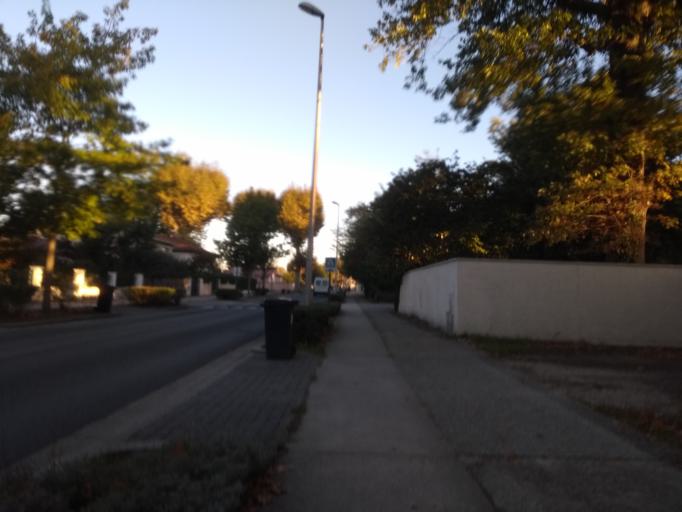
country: FR
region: Aquitaine
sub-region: Departement de la Gironde
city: Pessac
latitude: 44.7968
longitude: -0.6306
